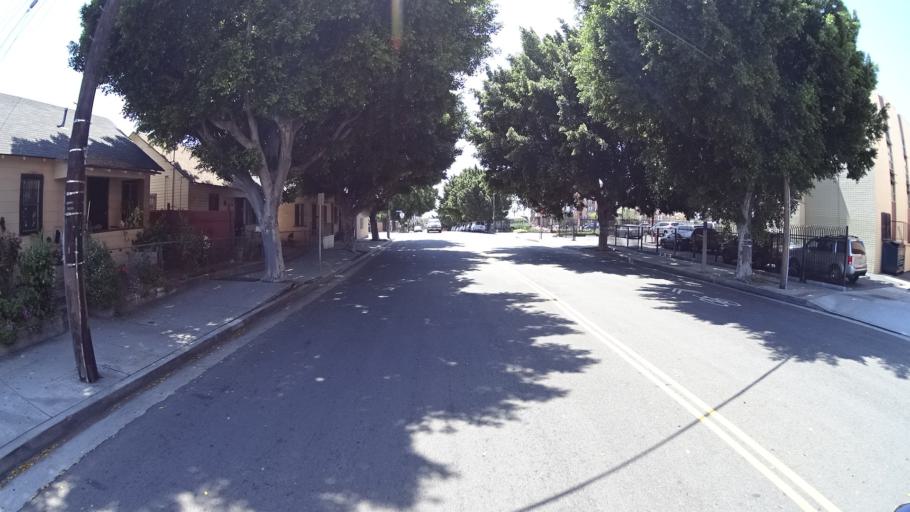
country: US
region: California
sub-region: Los Angeles County
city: Boyle Heights
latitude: 34.0496
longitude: -118.2155
